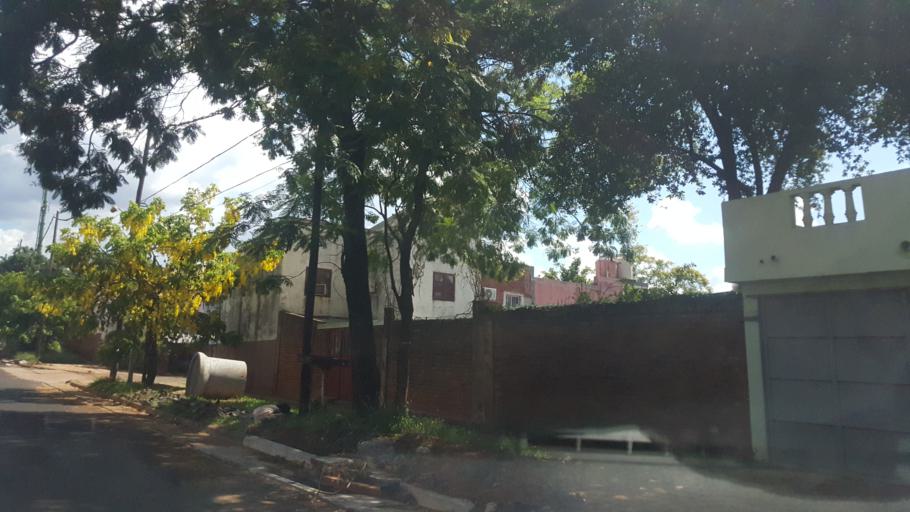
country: AR
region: Misiones
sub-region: Departamento de Capital
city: Posadas
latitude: -27.3583
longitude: -55.9229
